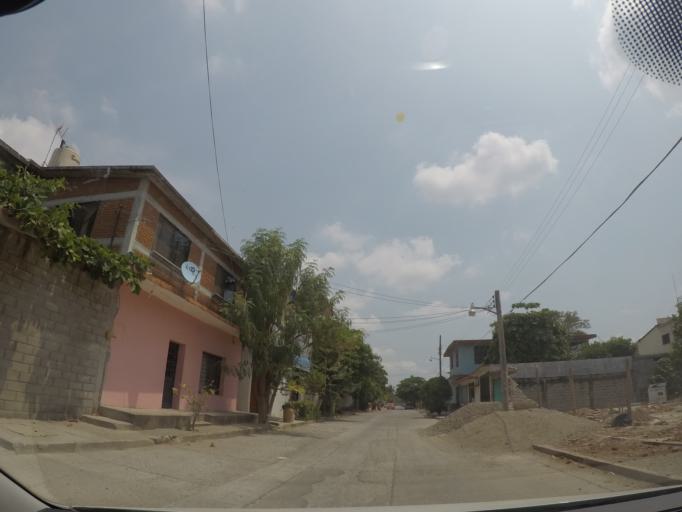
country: MX
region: Oaxaca
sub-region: El Espinal
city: El Espinal
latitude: 16.4893
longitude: -95.0424
